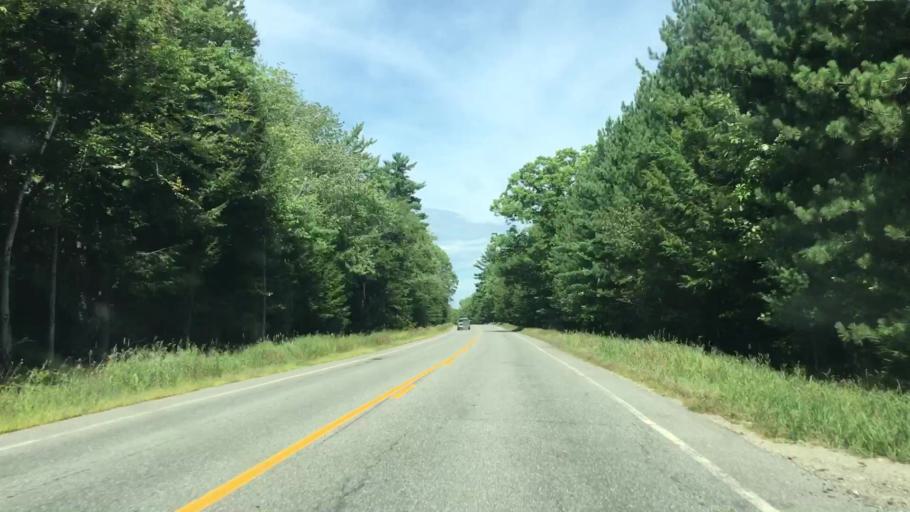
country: US
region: Maine
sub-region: Penobscot County
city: Lincoln
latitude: 45.3754
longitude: -68.5522
